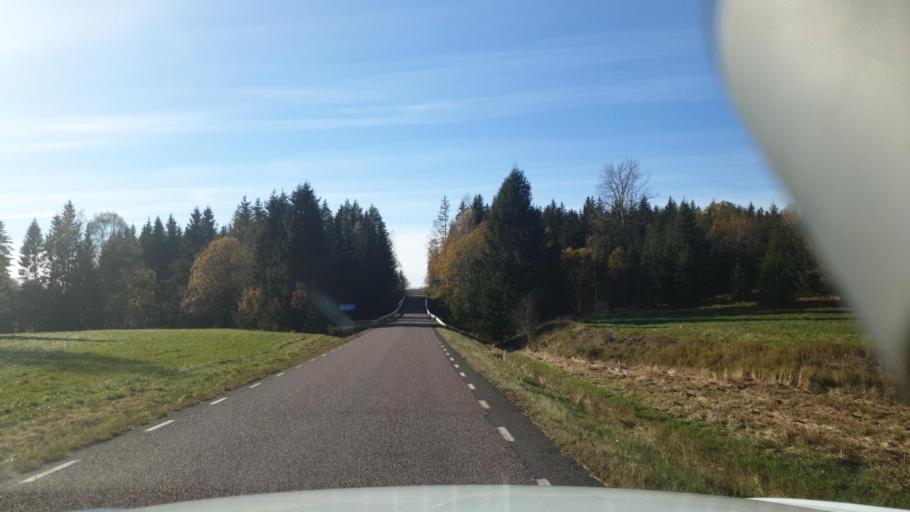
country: SE
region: Vaermland
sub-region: Karlstads Kommun
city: Edsvalla
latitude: 59.4954
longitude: 13.1044
